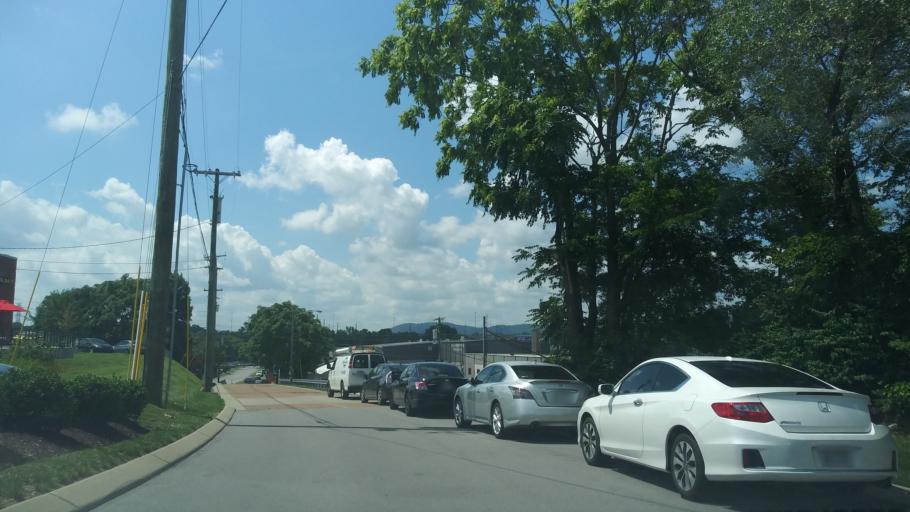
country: US
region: Tennessee
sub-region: Davidson County
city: Nashville
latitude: 36.1279
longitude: -86.7706
